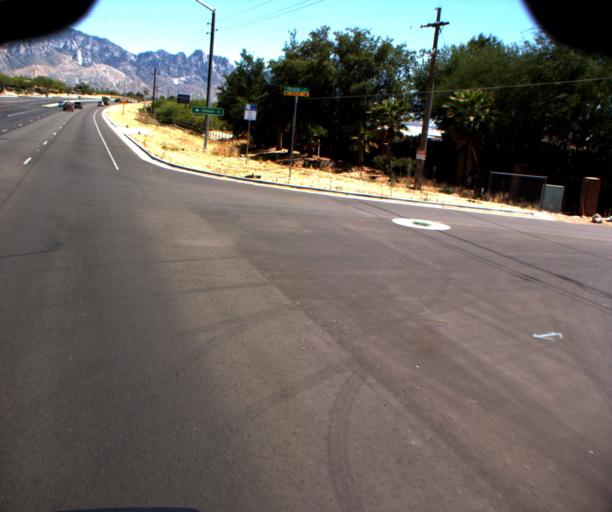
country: US
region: Arizona
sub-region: Pima County
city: Catalina
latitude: 32.4864
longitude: -110.9233
